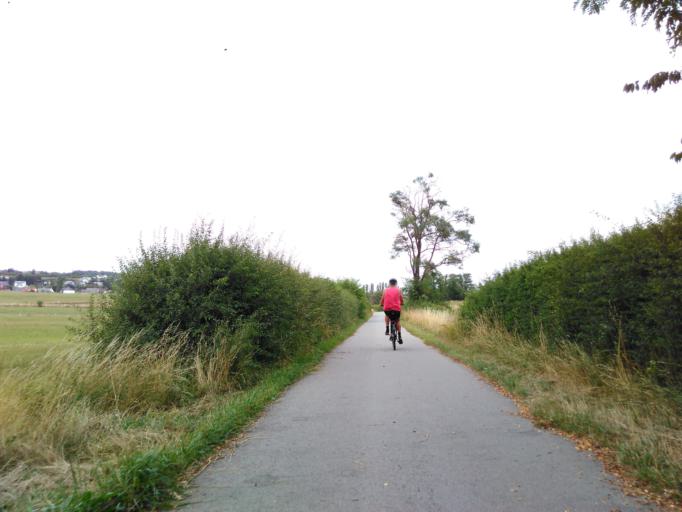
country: LU
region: Grevenmacher
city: Gonderange
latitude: 49.6865
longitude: 6.2496
